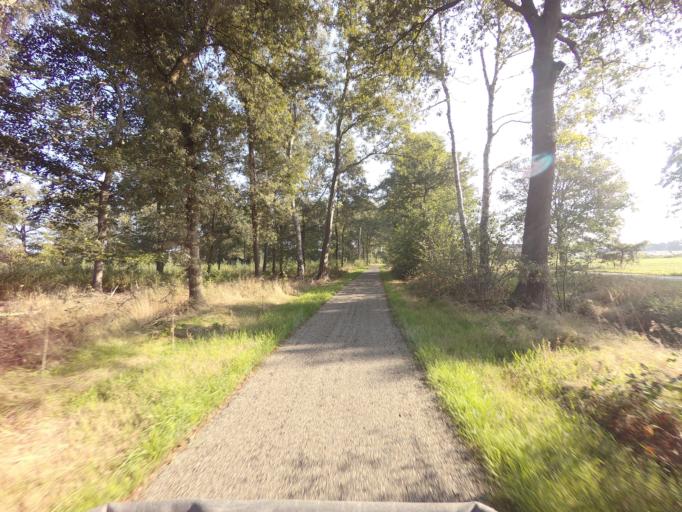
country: NL
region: Overijssel
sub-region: Gemeente Raalte
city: Raalte
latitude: 52.3116
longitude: 6.2761
